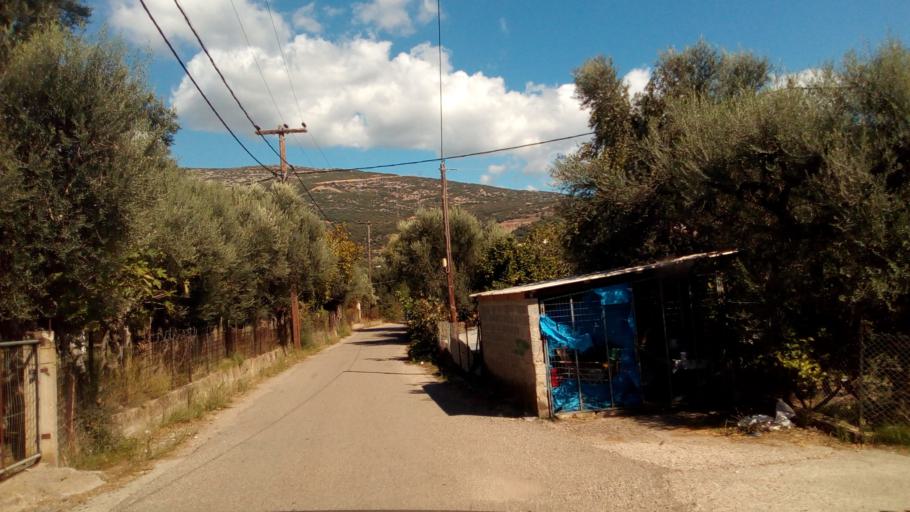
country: GR
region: West Greece
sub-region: Nomos Aitolias kai Akarnanias
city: Nafpaktos
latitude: 38.3888
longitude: 21.8073
